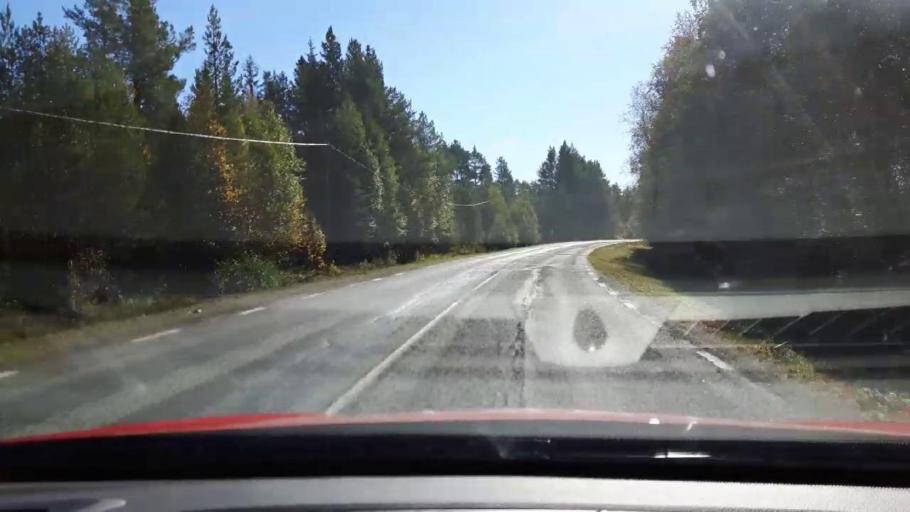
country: SE
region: Jaemtland
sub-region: Harjedalens Kommun
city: Sveg
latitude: 62.3343
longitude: 14.0536
